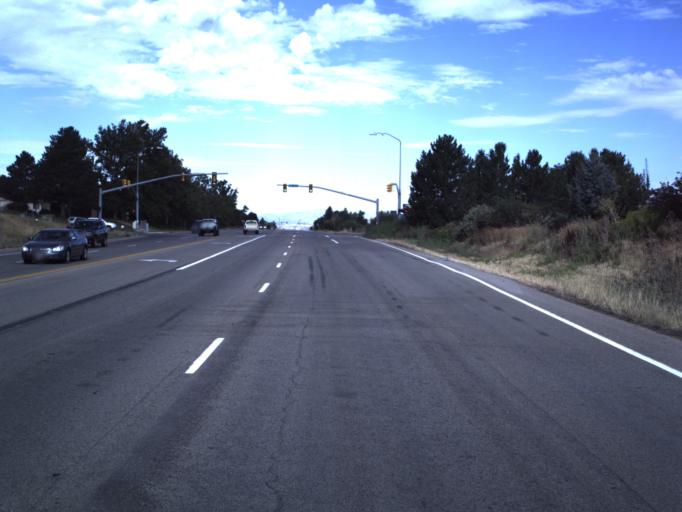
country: US
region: Utah
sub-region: Weber County
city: Washington Terrace
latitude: 41.1628
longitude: -111.9508
